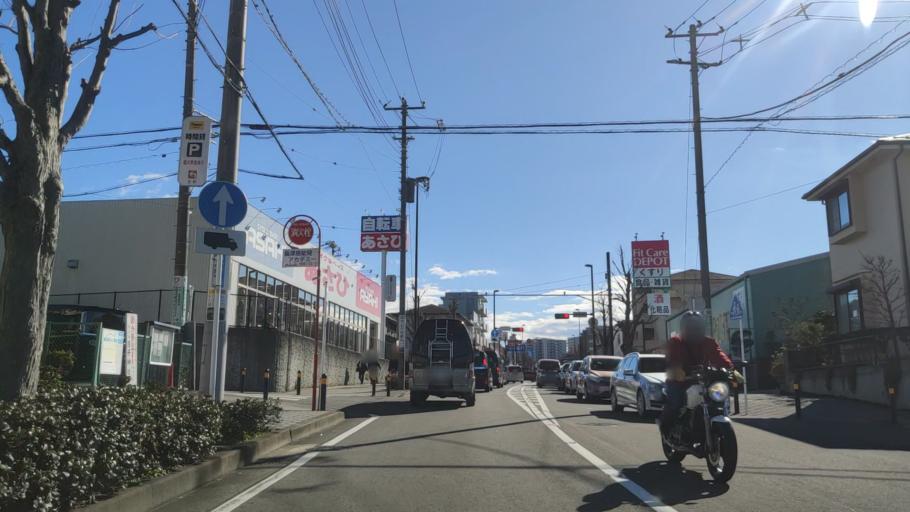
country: JP
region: Tokyo
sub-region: Machida-shi
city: Machida
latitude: 35.5266
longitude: 139.4981
